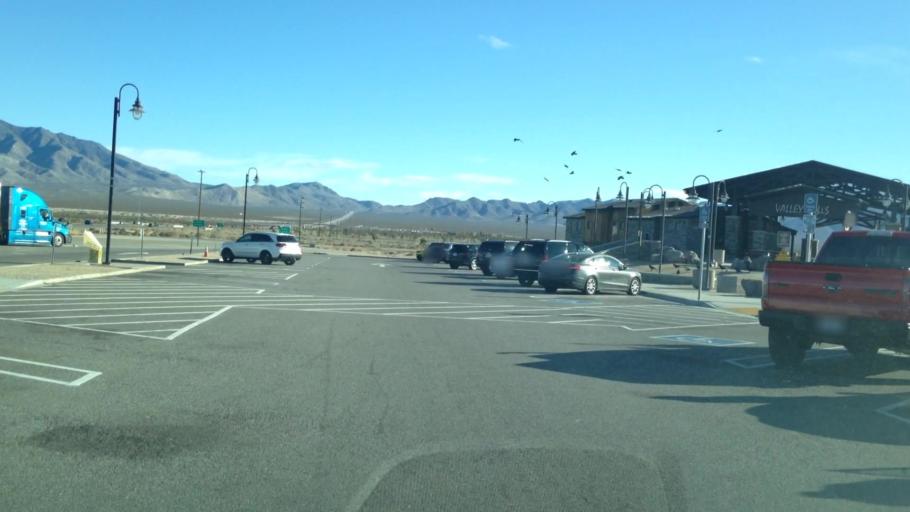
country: US
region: Nevada
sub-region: Clark County
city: Sandy Valley
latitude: 35.4339
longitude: -115.7002
